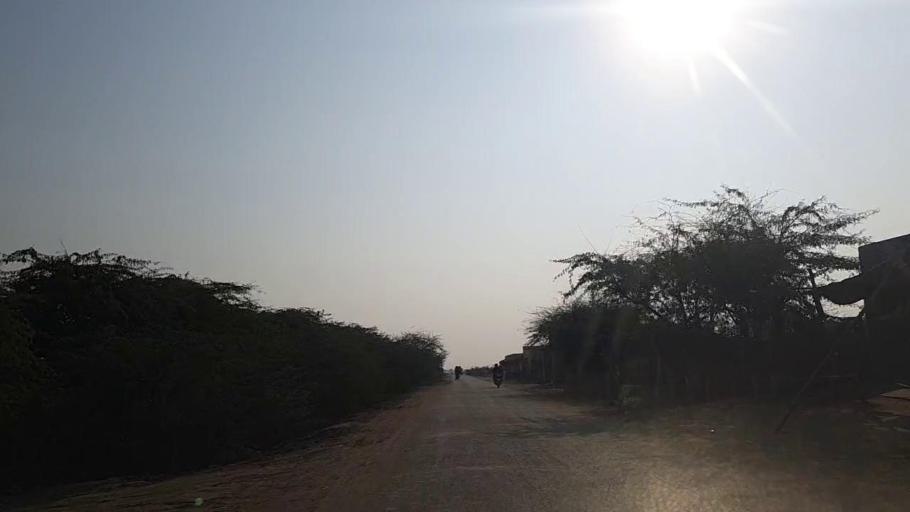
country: PK
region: Sindh
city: Jam Sahib
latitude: 26.2918
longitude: 68.6273
